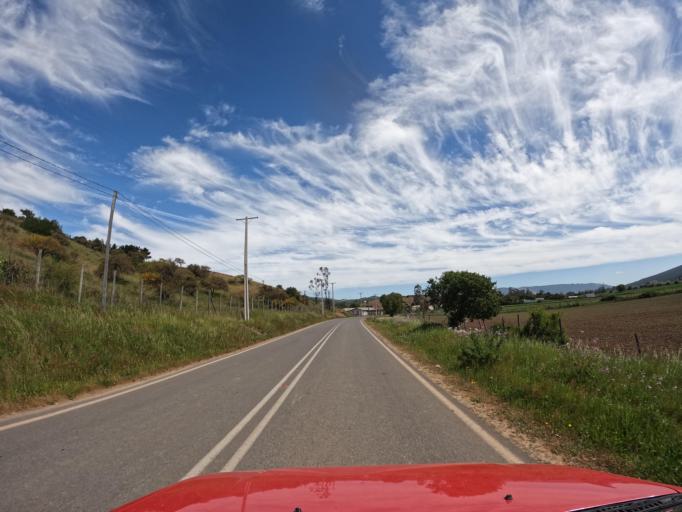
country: CL
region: Maule
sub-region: Provincia de Talca
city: Constitucion
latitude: -35.0006
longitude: -72.0251
